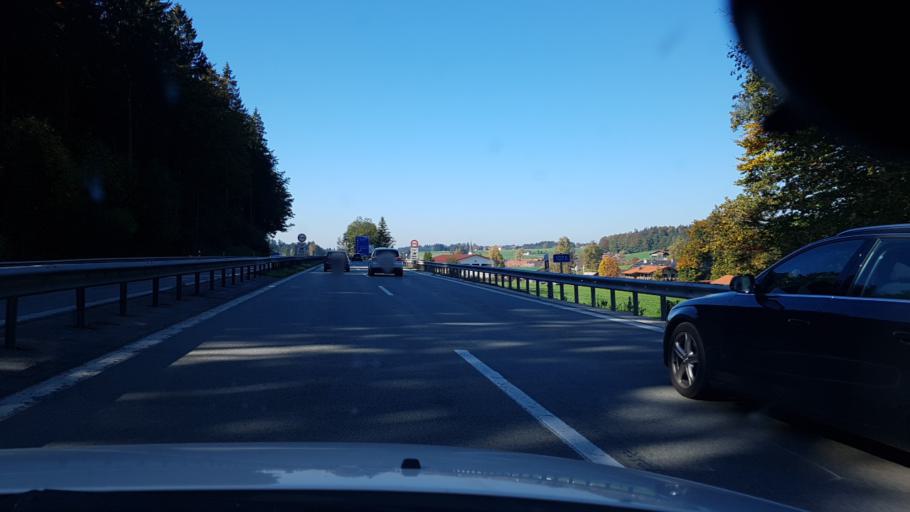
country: DE
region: Bavaria
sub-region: Upper Bavaria
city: Inzell
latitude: 47.8284
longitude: 12.7492
